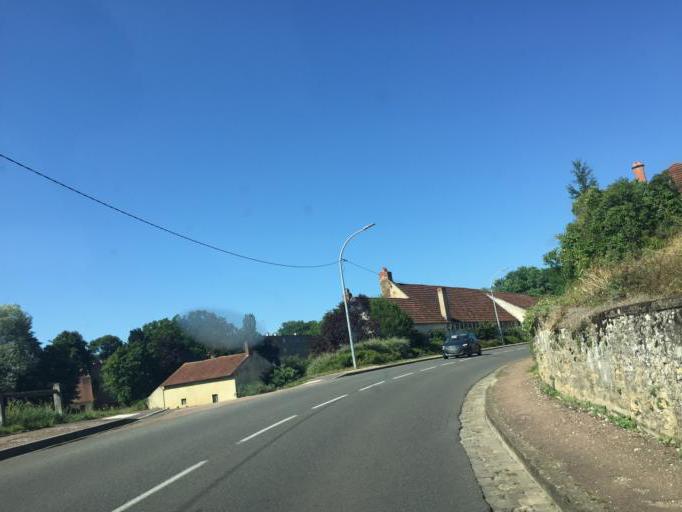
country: FR
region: Bourgogne
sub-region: Departement de la Nievre
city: Clamecy
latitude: 47.4570
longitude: 3.5146
